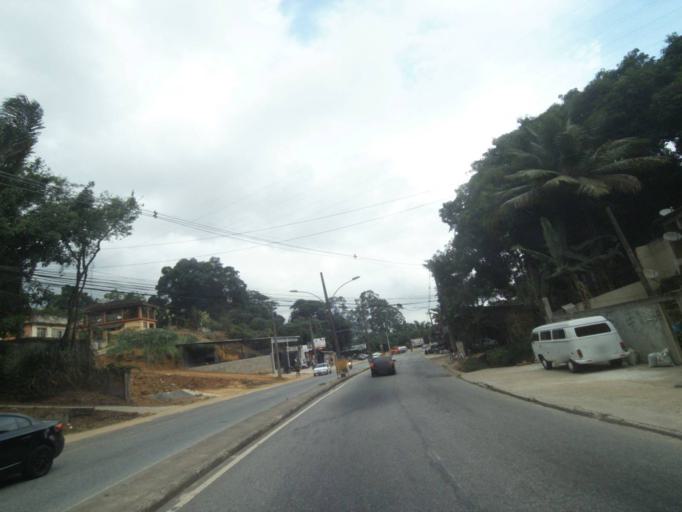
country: BR
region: Rio de Janeiro
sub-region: Sao Joao De Meriti
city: Sao Joao de Meriti
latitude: -22.9048
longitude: -43.3800
